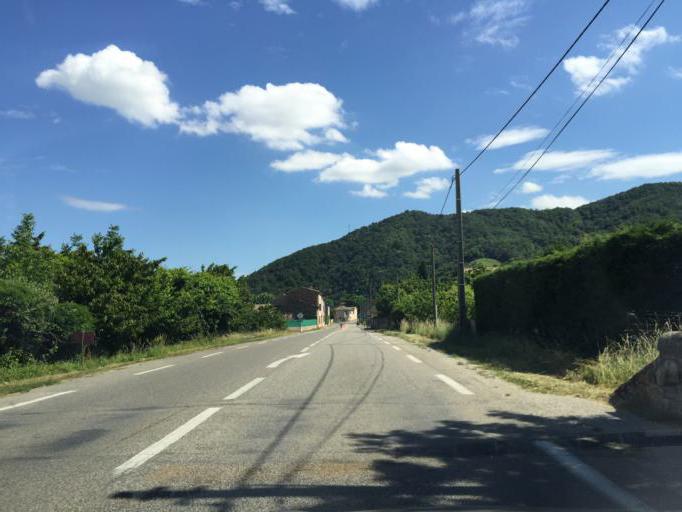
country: FR
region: Rhone-Alpes
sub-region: Departement de l'Ardeche
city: Saint-Jean-de-Muzols
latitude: 45.1150
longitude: 4.8042
